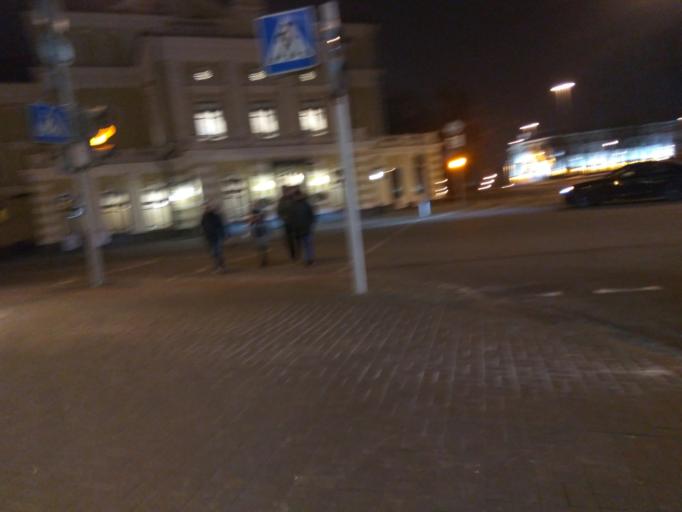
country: BY
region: Minsk
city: Minsk
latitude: 53.9001
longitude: 27.5626
